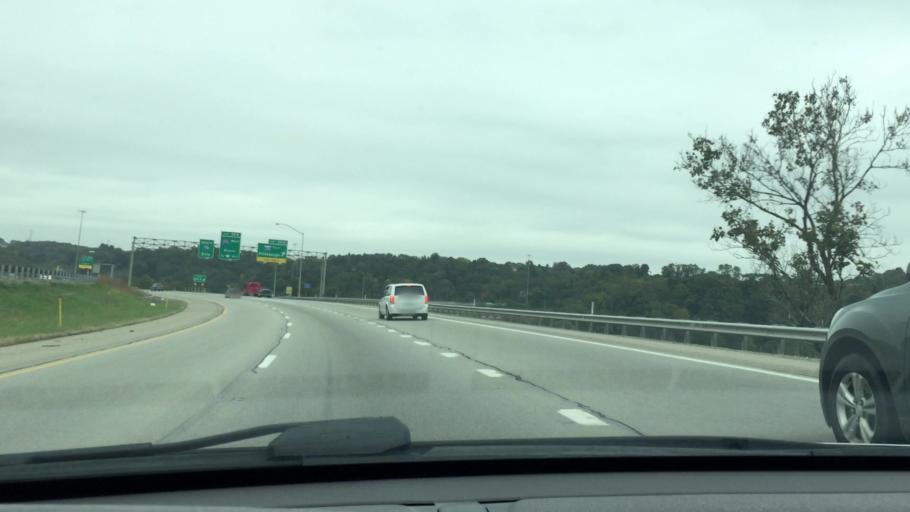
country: US
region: Pennsylvania
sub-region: Allegheny County
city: Carnegie
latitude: 40.4179
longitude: -80.1029
